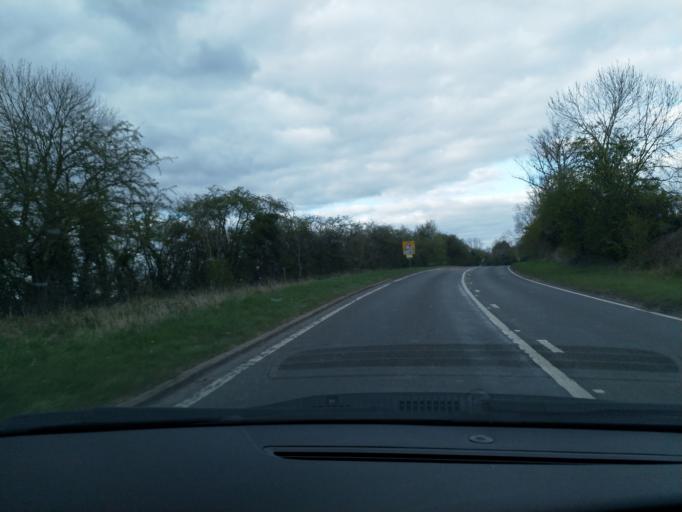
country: GB
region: England
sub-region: Warwickshire
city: Royal Leamington Spa
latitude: 52.2523
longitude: -1.5388
